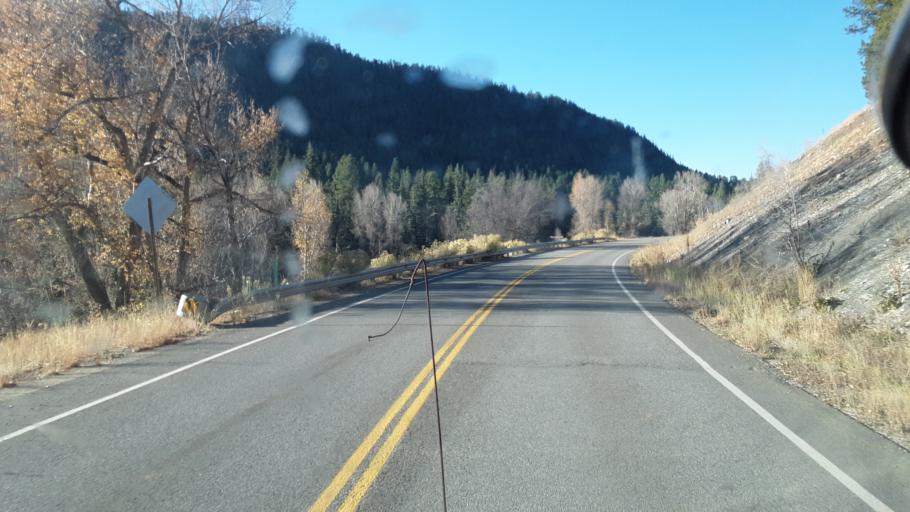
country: US
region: Colorado
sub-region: La Plata County
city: Bayfield
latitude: 37.3552
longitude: -107.6803
